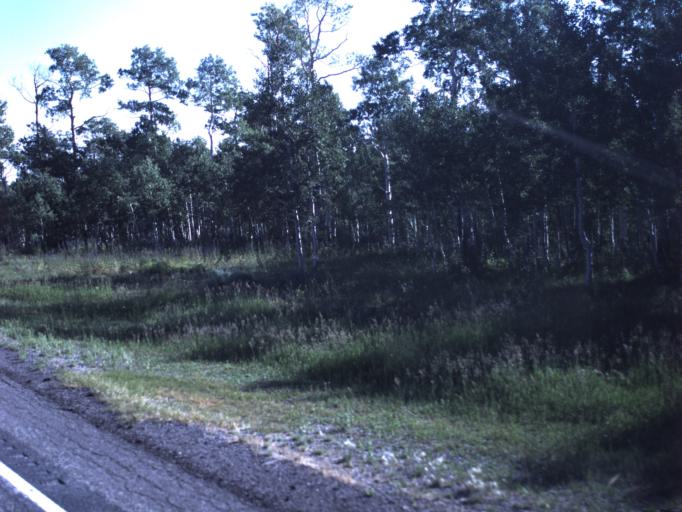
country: US
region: Utah
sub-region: Sanpete County
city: Fairview
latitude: 39.6546
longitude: -111.3302
